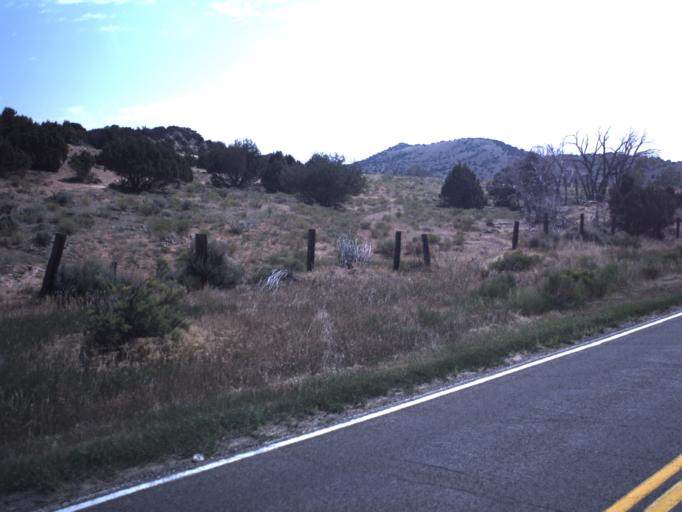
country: US
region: Utah
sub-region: Daggett County
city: Manila
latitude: 40.9771
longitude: -109.7778
